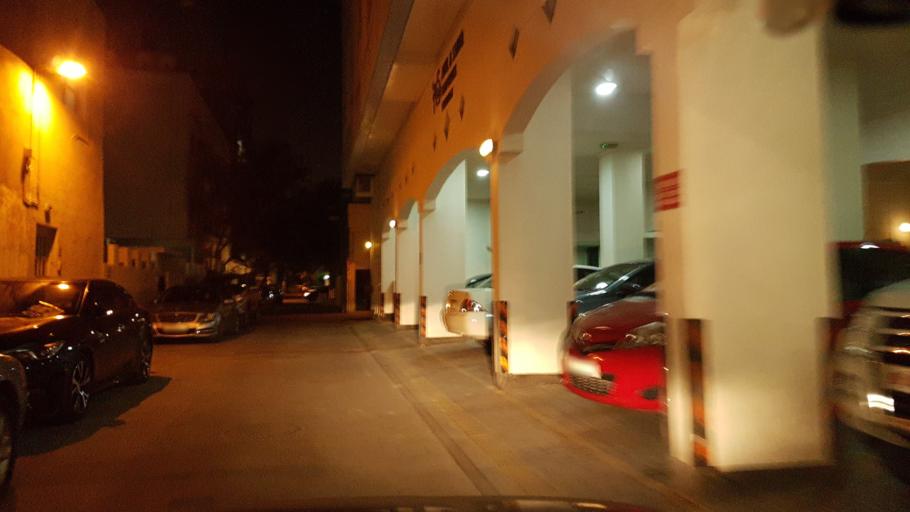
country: BH
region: Manama
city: Manama
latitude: 26.2167
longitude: 50.5869
